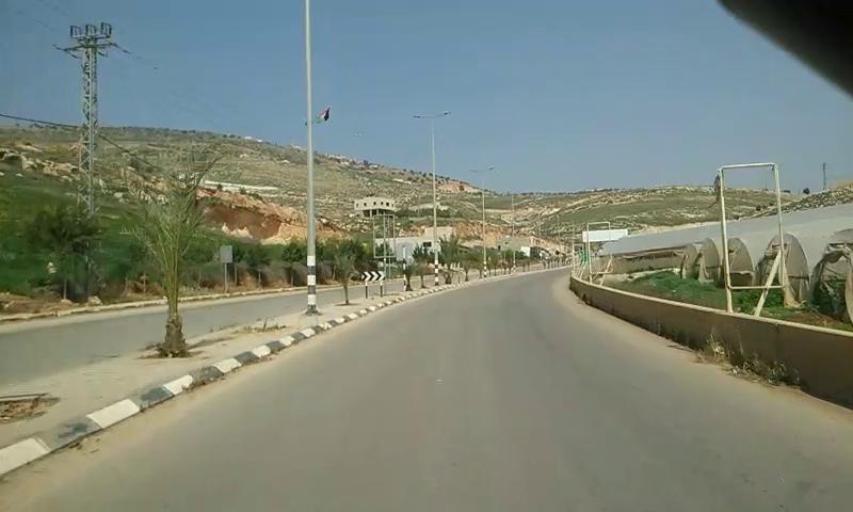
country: PS
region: West Bank
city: Tubas
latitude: 32.3063
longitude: 35.3639
